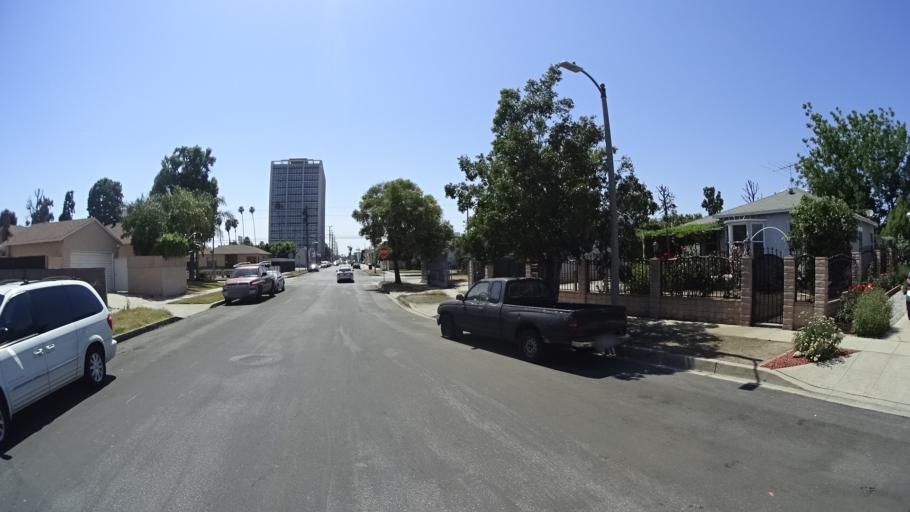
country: US
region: California
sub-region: Los Angeles County
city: Van Nuys
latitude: 34.2198
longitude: -118.4469
